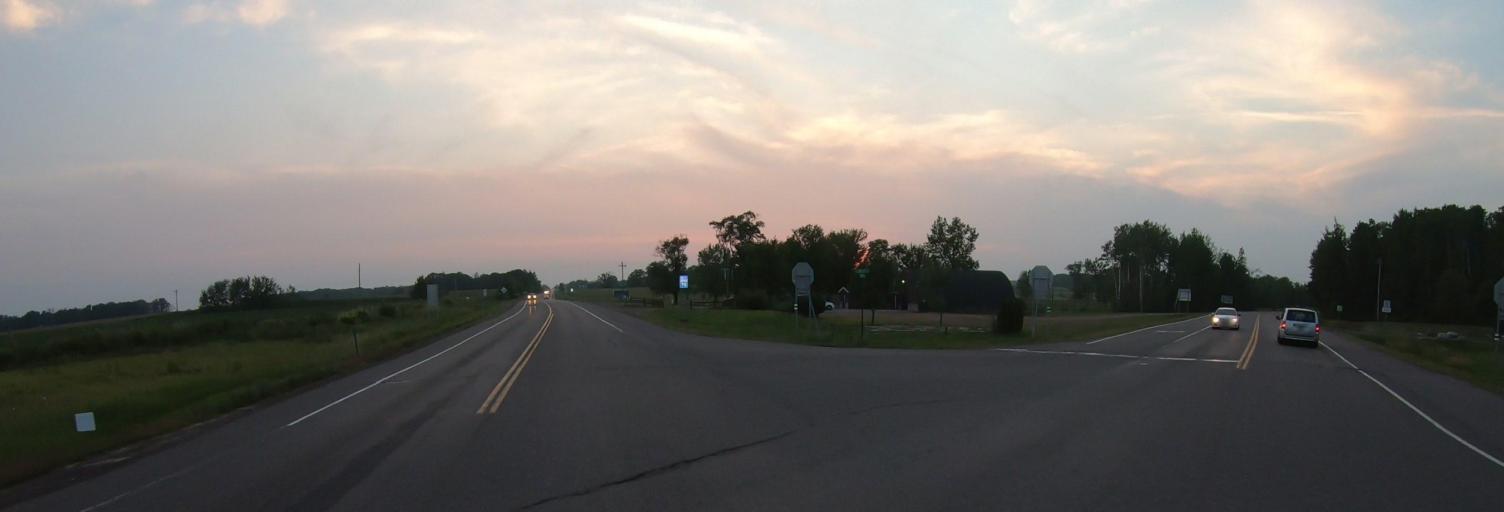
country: US
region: Minnesota
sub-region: Pine County
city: Rock Creek
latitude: 45.7665
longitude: -92.9675
